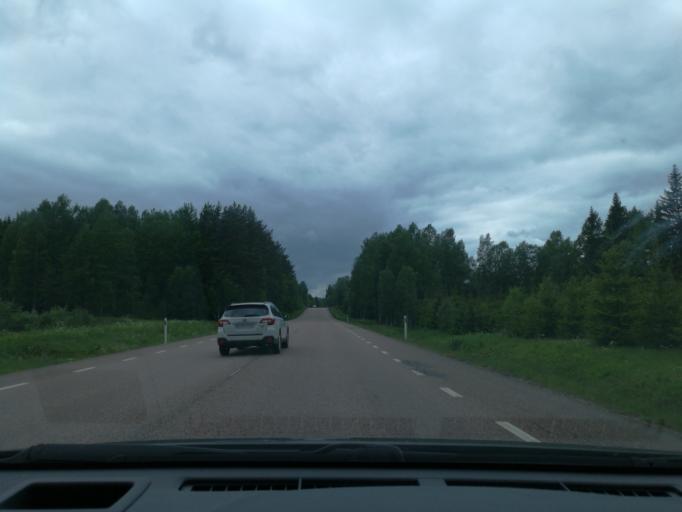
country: SE
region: Dalarna
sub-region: Smedjebackens Kommun
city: Smedjebacken
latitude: 60.1404
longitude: 15.3560
